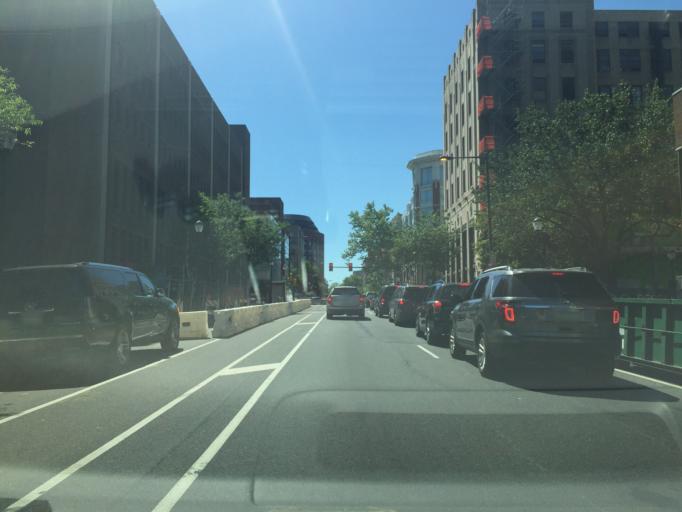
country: US
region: Pennsylvania
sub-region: Philadelphia County
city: Philadelphia
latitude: 39.9530
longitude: -75.1939
